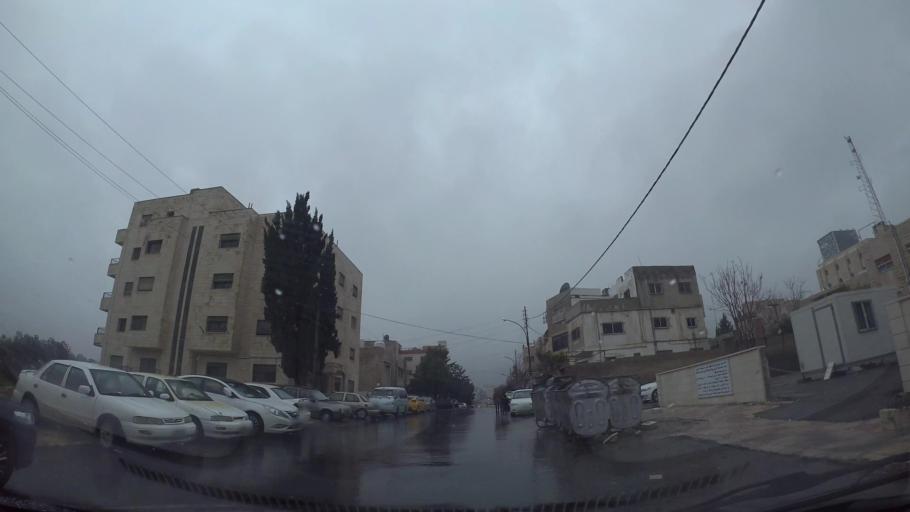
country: JO
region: Amman
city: Amman
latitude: 31.9592
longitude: 35.9094
